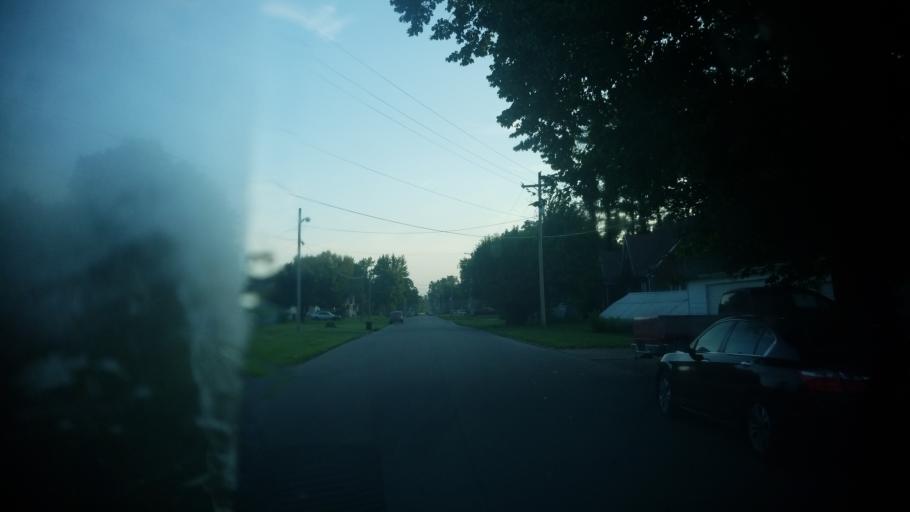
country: US
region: Illinois
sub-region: Wayne County
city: Fairfield
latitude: 38.3815
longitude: -88.3719
